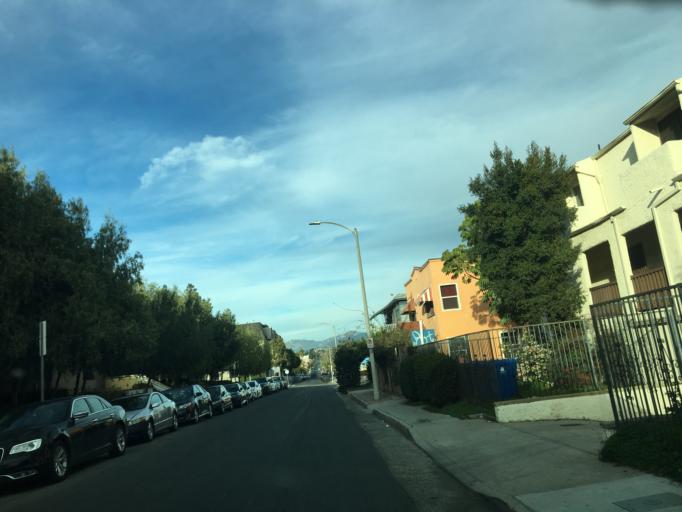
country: US
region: California
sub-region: Los Angeles County
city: Echo Park
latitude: 34.0658
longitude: -118.2803
